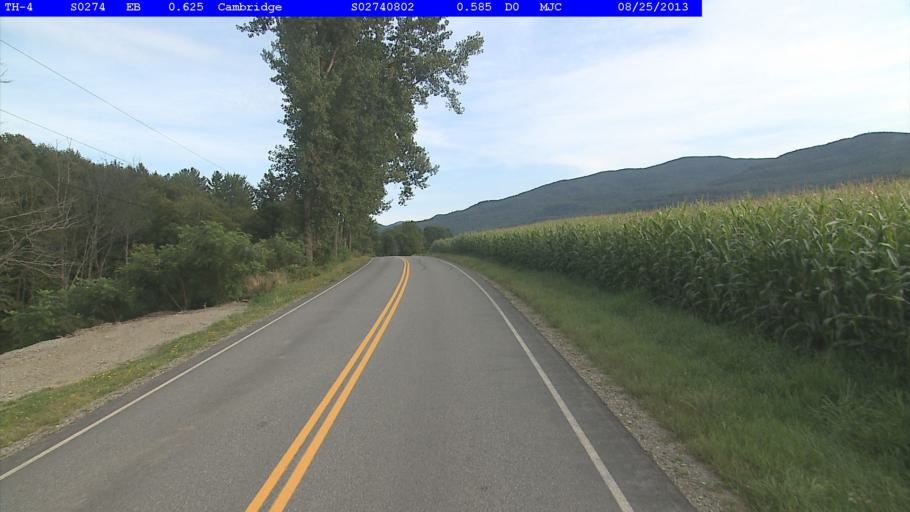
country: US
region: Vermont
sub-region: Lamoille County
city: Johnson
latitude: 44.6747
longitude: -72.7682
